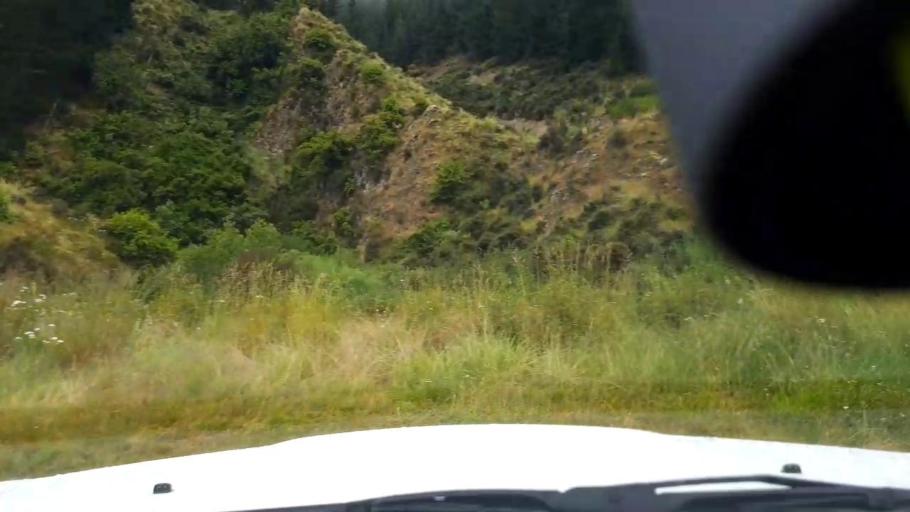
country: NZ
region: Canterbury
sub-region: Timaru District
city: Pleasant Point
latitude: -44.0329
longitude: 170.9901
